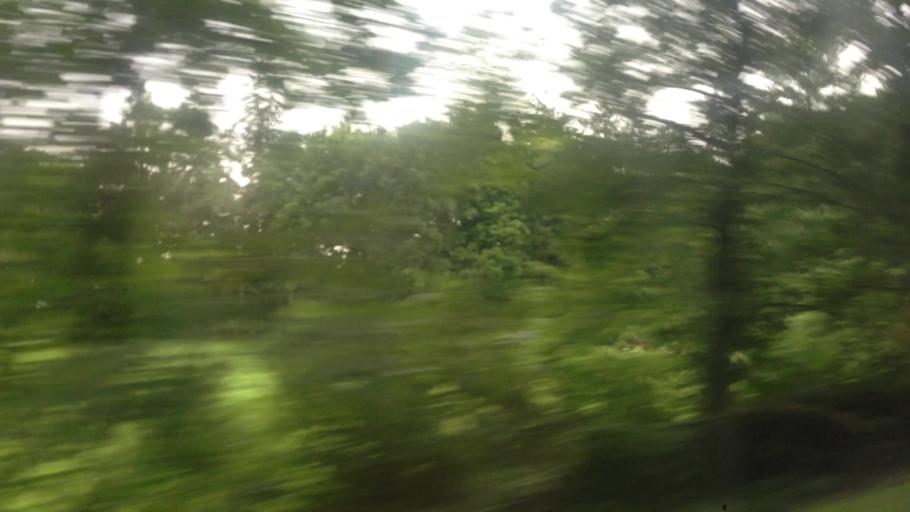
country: US
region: New York
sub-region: Dutchess County
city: Red Hook
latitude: 41.9843
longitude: -73.9158
